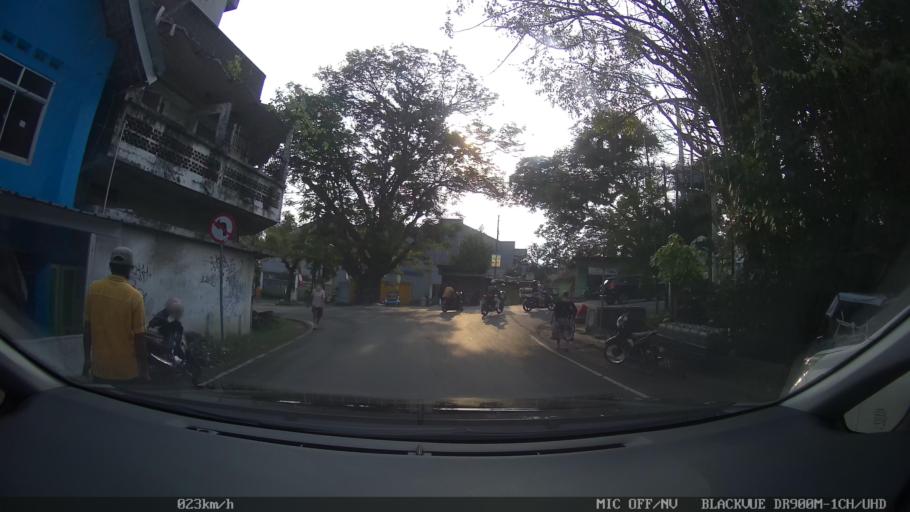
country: ID
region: Lampung
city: Bandarlampung
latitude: -5.4472
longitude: 105.2630
